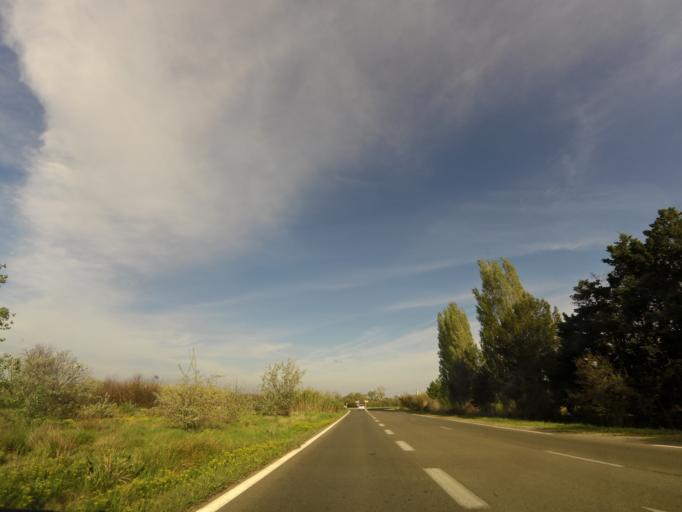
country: FR
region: Languedoc-Roussillon
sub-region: Departement de l'Herault
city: La Grande-Motte
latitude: 43.5758
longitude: 4.1007
